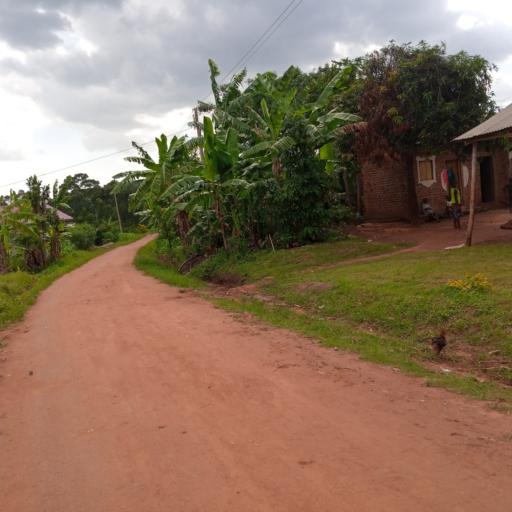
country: UG
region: Eastern Region
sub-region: Mbale District
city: Mbale
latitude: 1.1241
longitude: 34.1815
